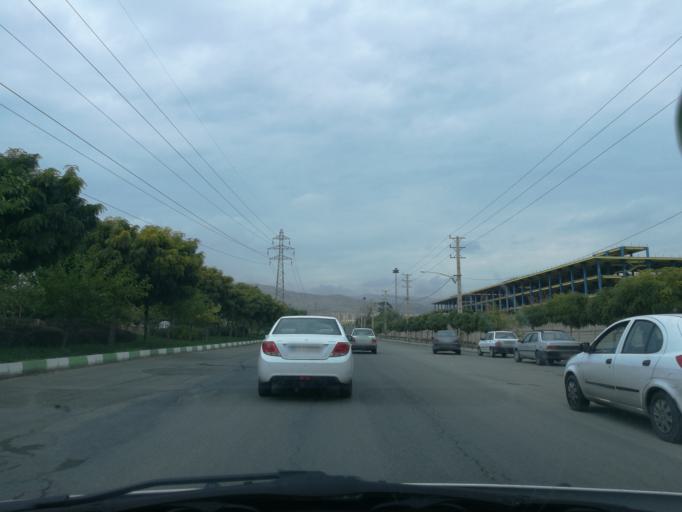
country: IR
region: Alborz
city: Karaj
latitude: 35.8559
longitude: 50.9214
